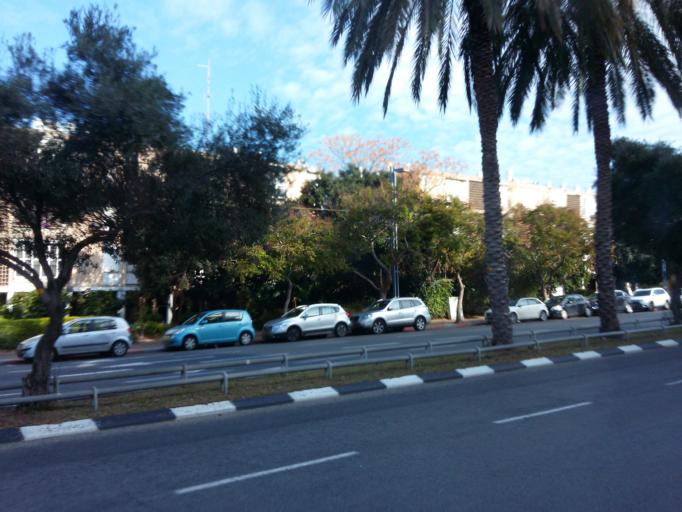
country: IL
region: Tel Aviv
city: Ramat Gan
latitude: 32.1130
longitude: 34.7955
